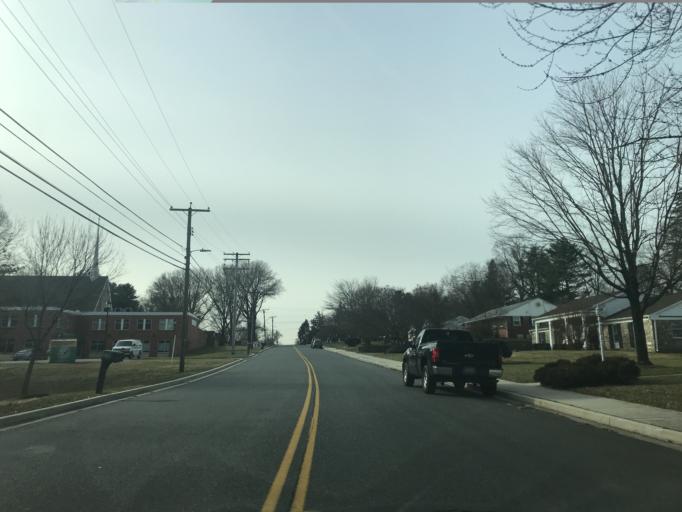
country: US
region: Maryland
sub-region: Harford County
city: Aberdeen
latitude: 39.5189
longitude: -76.1648
